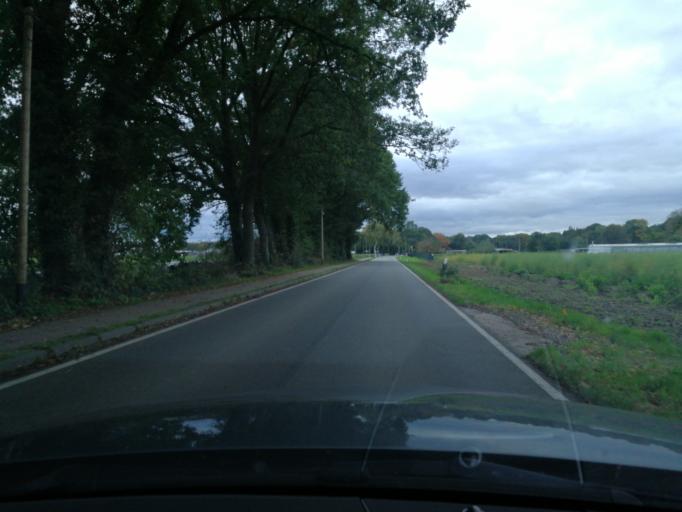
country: NL
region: Limburg
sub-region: Gemeente Venlo
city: Arcen
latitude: 51.4881
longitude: 6.2214
